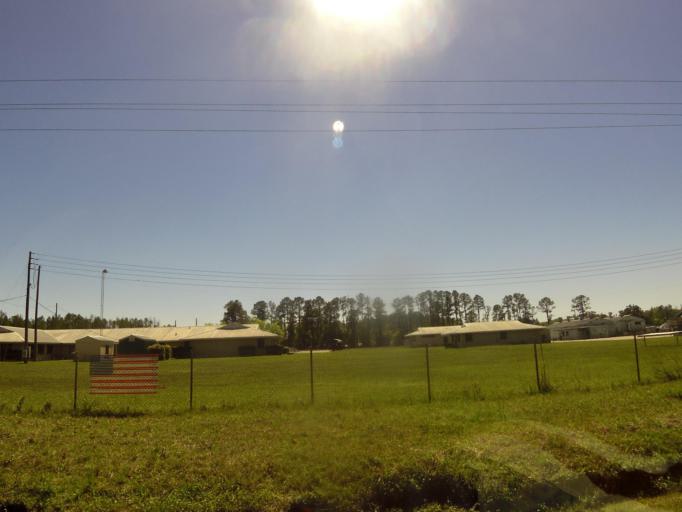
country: US
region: Florida
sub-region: Bradford County
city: Starke
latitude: 30.0559
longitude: -82.0501
